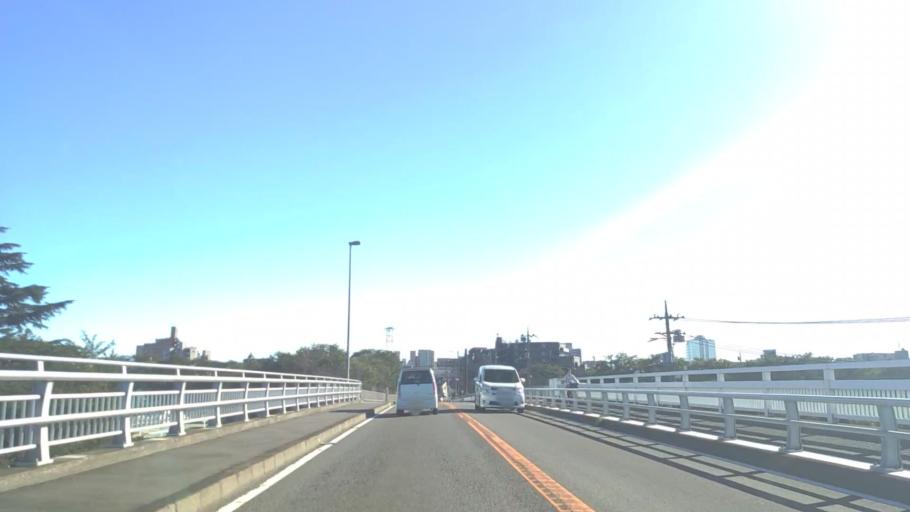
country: JP
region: Kanagawa
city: Atsugi
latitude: 35.4511
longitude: 139.3658
